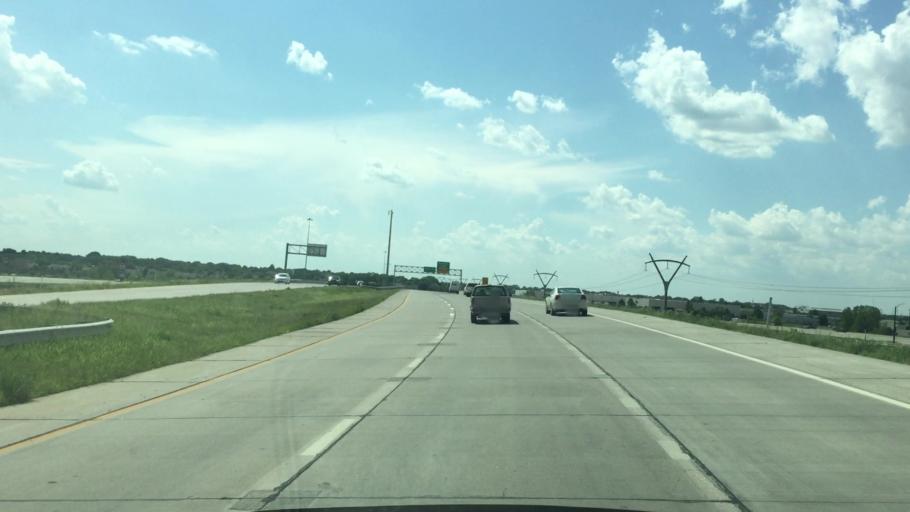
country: US
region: Kansas
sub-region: Sedgwick County
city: Bellaire
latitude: 37.7299
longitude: -97.2052
